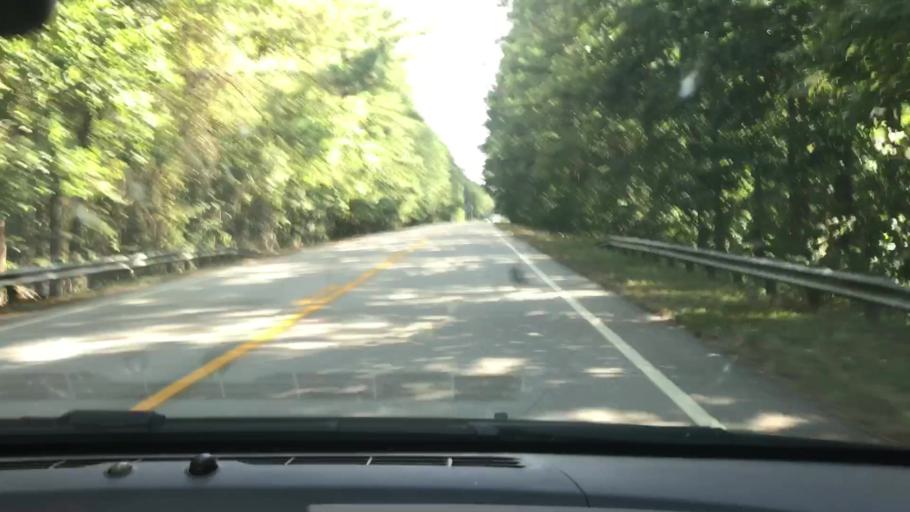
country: US
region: Georgia
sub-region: Troup County
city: La Grange
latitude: 33.1271
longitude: -85.0894
